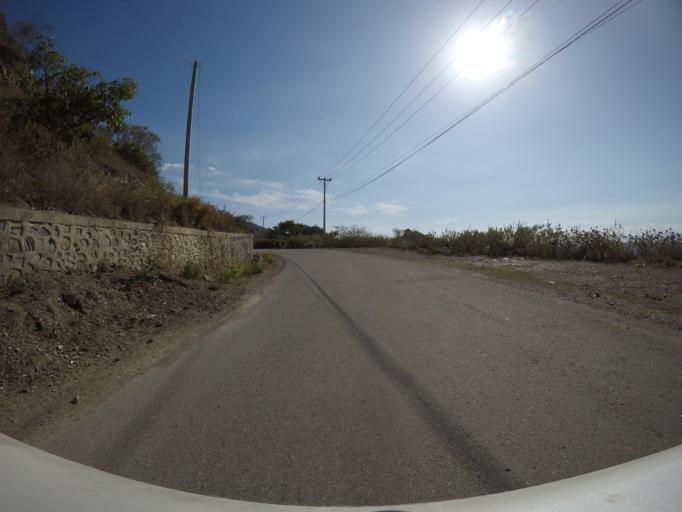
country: TL
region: Liquica
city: Maubara
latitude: -8.6322
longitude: 125.1487
